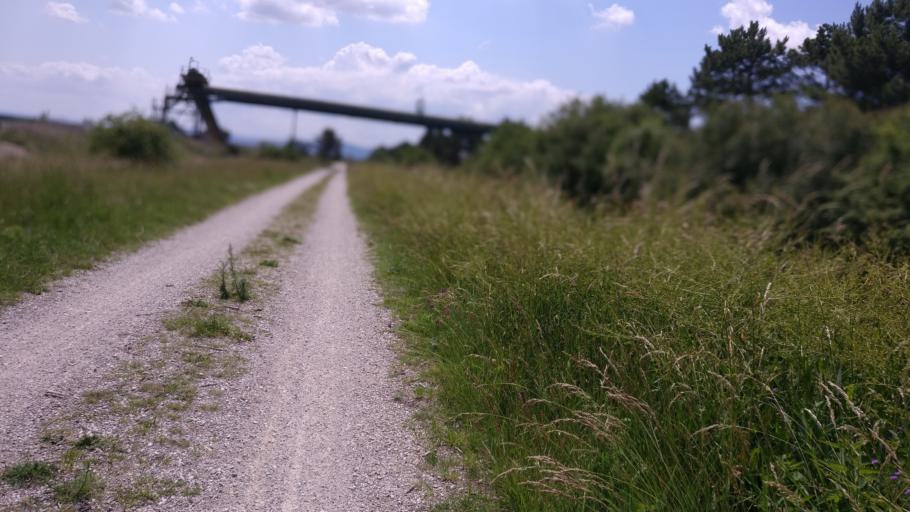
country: AT
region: Lower Austria
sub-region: Politischer Bezirk Wiener Neustadt
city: Sollenau
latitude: 47.8771
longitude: 16.2809
